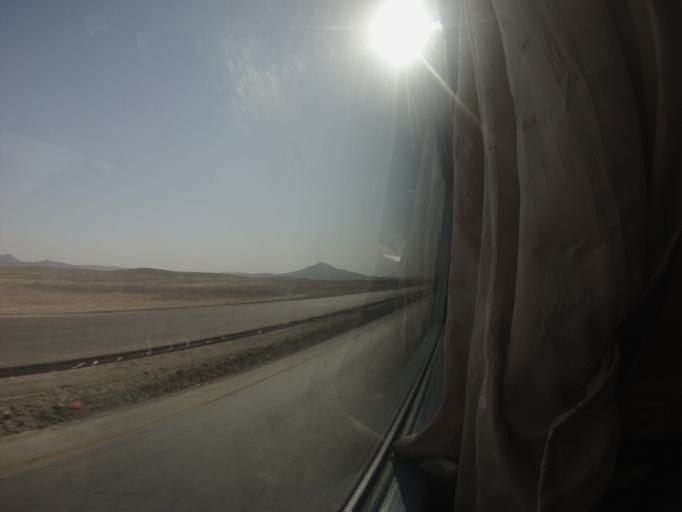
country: AZ
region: Sumqayit
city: Haci Zeynalabdin
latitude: 40.4941
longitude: 49.5232
